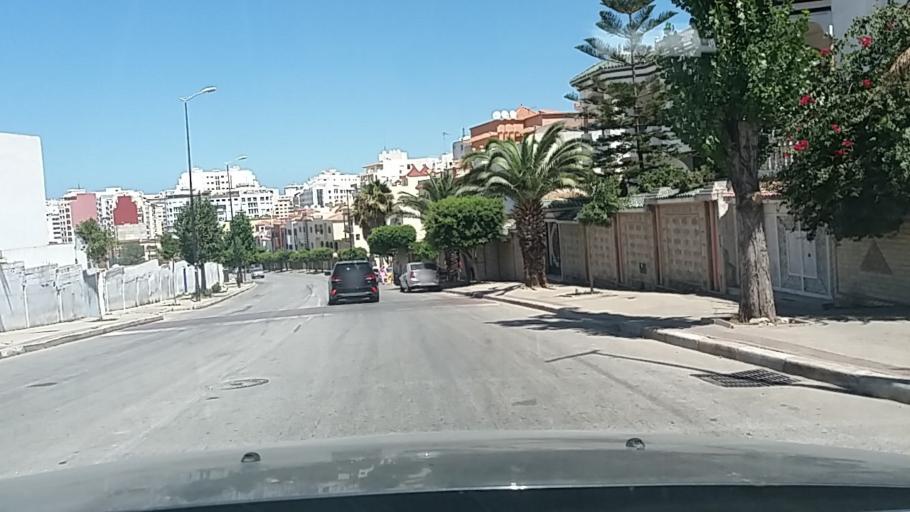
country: MA
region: Tanger-Tetouan
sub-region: Tanger-Assilah
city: Tangier
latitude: 35.7685
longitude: -5.7935
